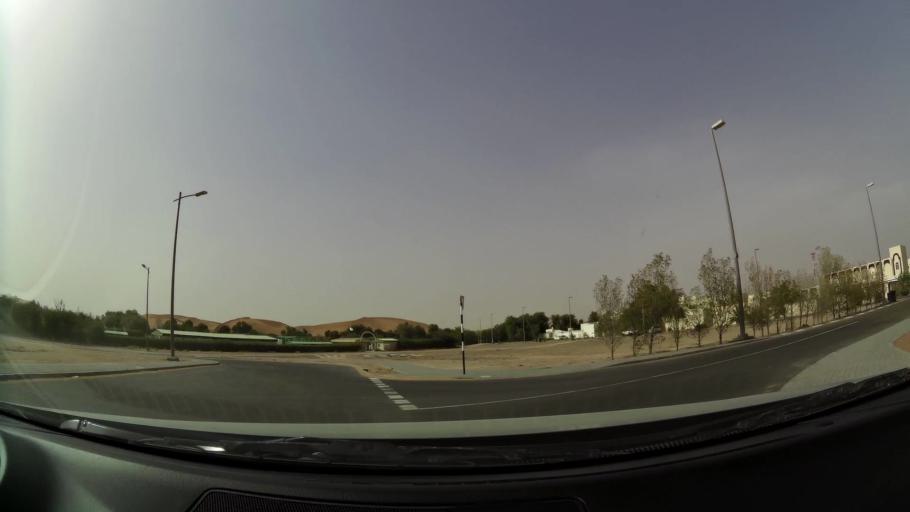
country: AE
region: Abu Dhabi
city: Al Ain
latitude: 24.2050
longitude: 55.5738
